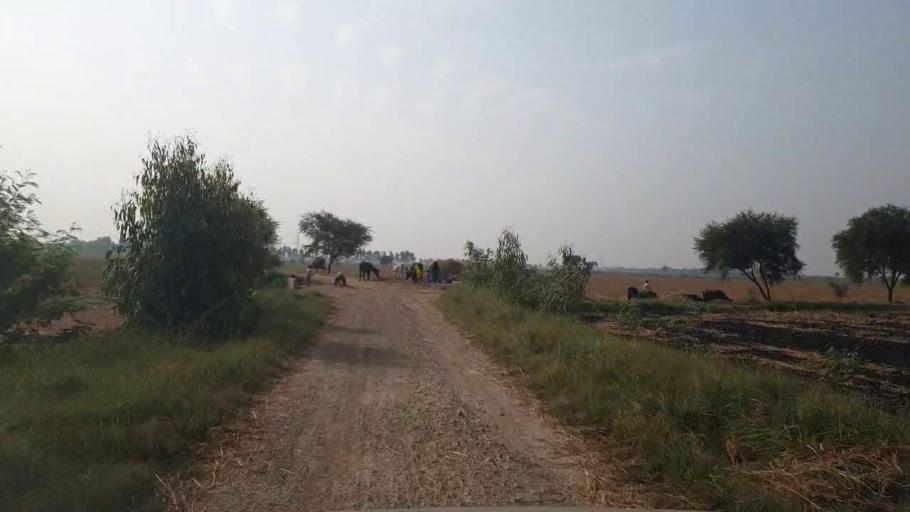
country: PK
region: Sindh
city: Tando Muhammad Khan
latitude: 25.1028
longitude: 68.5016
